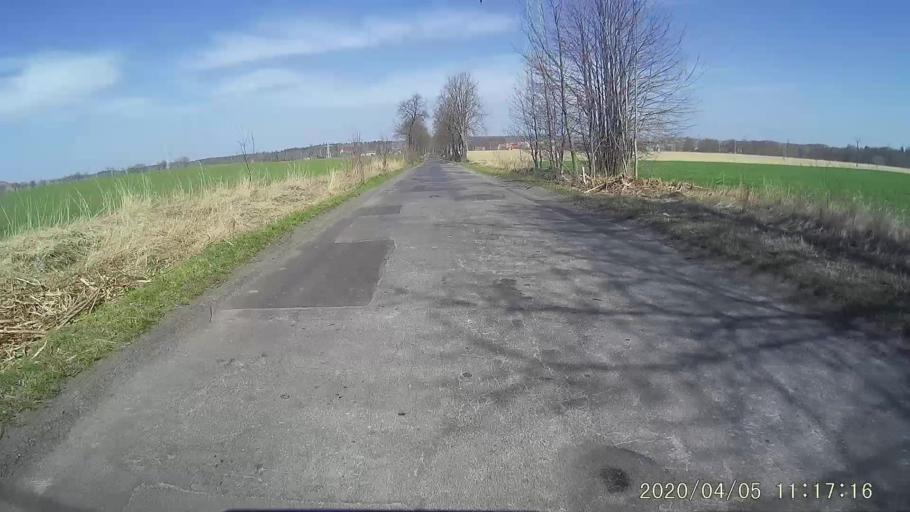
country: PL
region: Lower Silesian Voivodeship
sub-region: Powiat zgorzelecki
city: Sulikow
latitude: 51.0726
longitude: 15.1044
